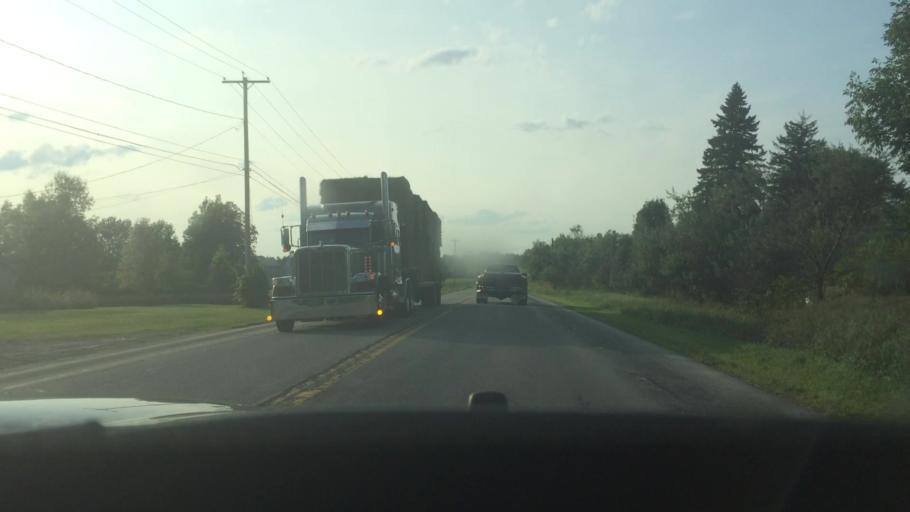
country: US
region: New York
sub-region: St. Lawrence County
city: Ogdensburg
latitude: 44.6787
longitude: -75.4404
